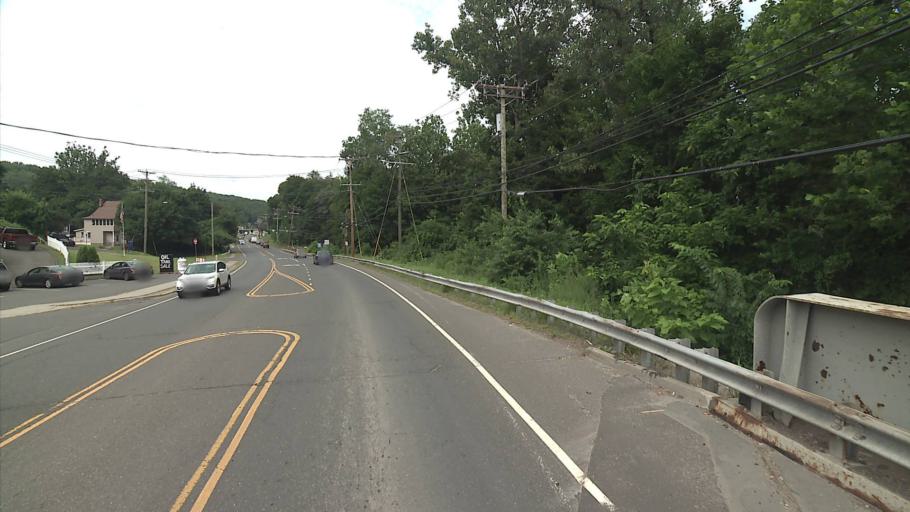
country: US
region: Connecticut
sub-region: New Haven County
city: Seymour
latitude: 41.3978
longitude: -73.0797
